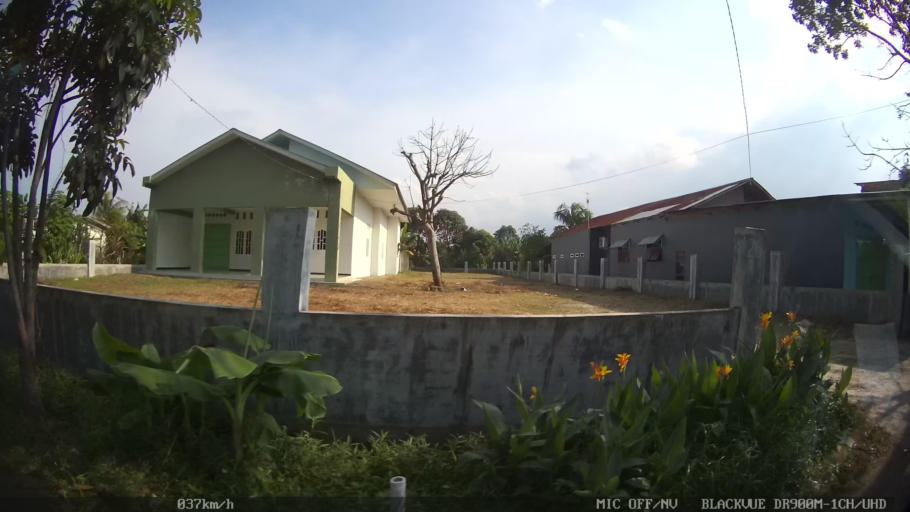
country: ID
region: North Sumatra
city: Percut
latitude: 3.5939
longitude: 98.7731
